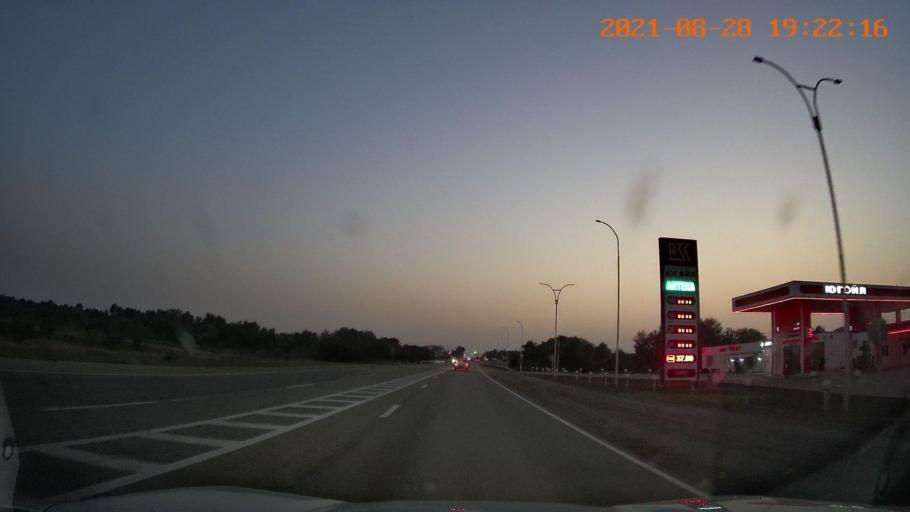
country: RU
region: Adygeya
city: Ponezhukay
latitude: 44.8779
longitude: 39.4641
